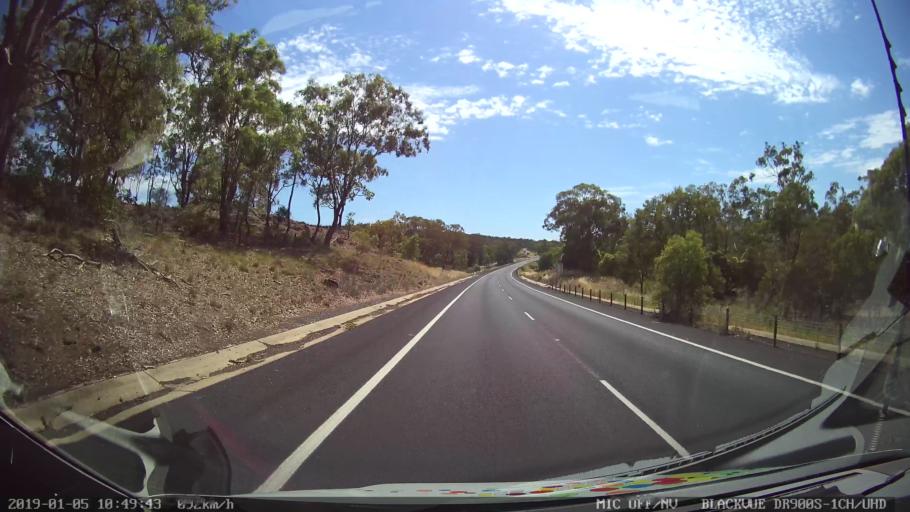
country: AU
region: New South Wales
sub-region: Warrumbungle Shire
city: Coonabarabran
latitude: -31.4322
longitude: 149.0646
